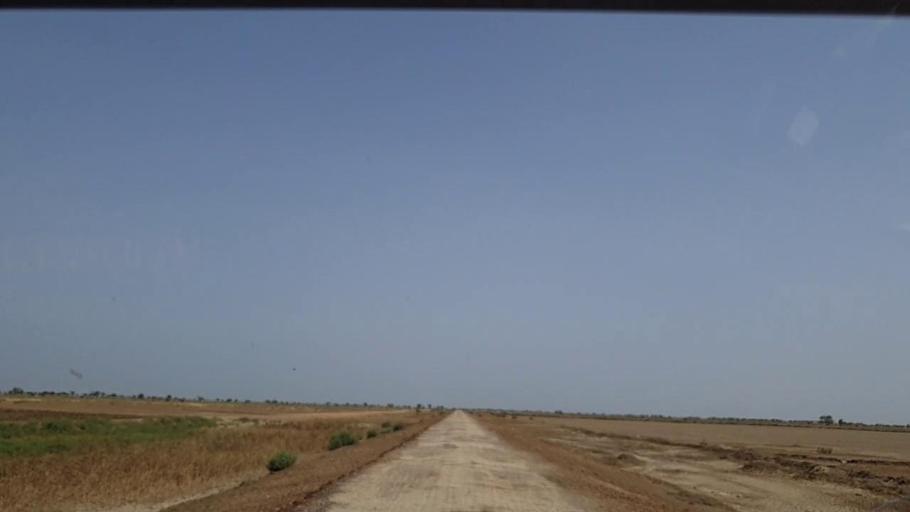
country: PK
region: Sindh
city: Johi
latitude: 26.7858
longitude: 67.6461
